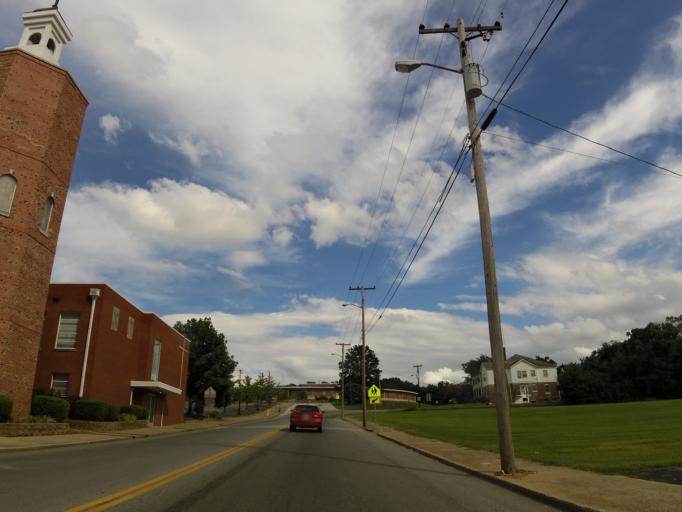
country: US
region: Kentucky
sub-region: Christian County
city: Hopkinsville
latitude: 36.8624
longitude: -87.4817
